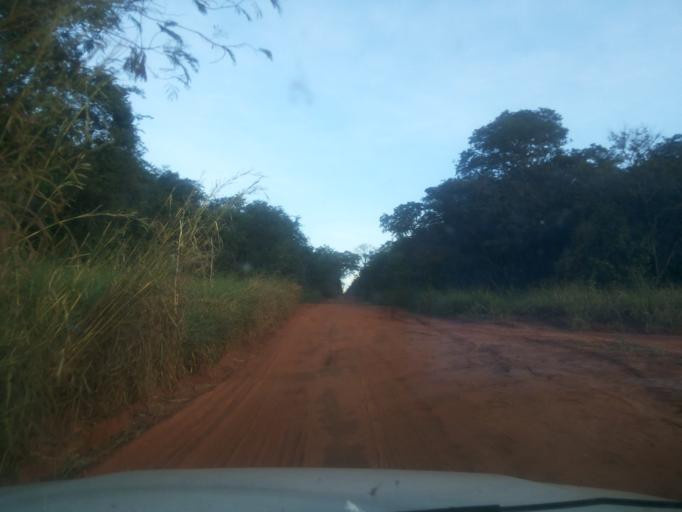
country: BR
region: Minas Gerais
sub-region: Santa Vitoria
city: Santa Vitoria
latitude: -19.0051
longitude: -50.3729
